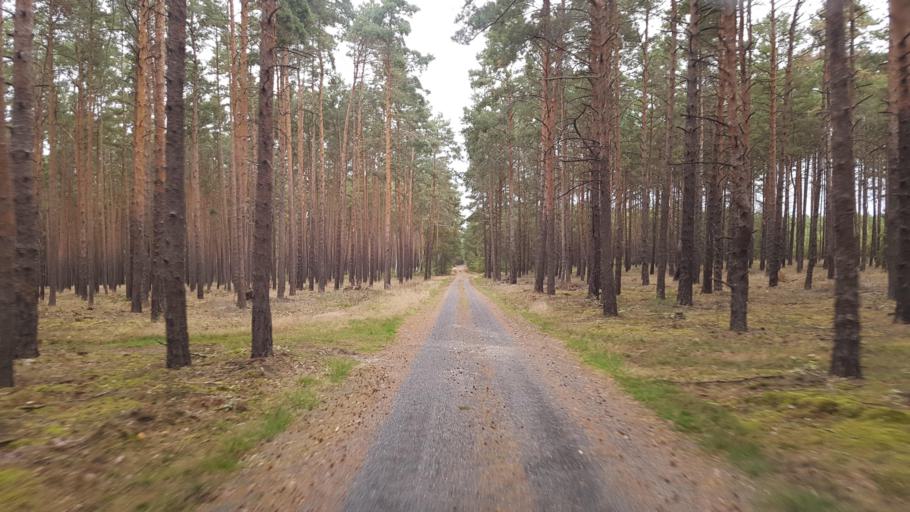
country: DE
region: Brandenburg
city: Sonnewalde
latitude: 51.7293
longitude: 13.6628
